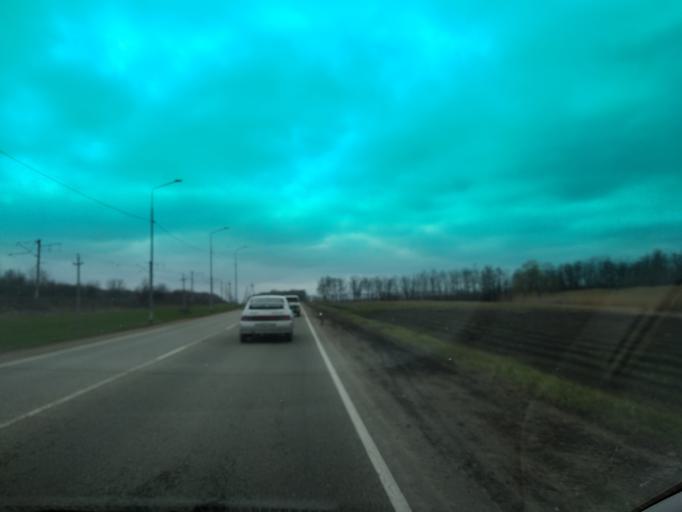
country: RU
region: Krasnodarskiy
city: Novorozhdestvenskaya
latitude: 45.8030
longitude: 39.9865
